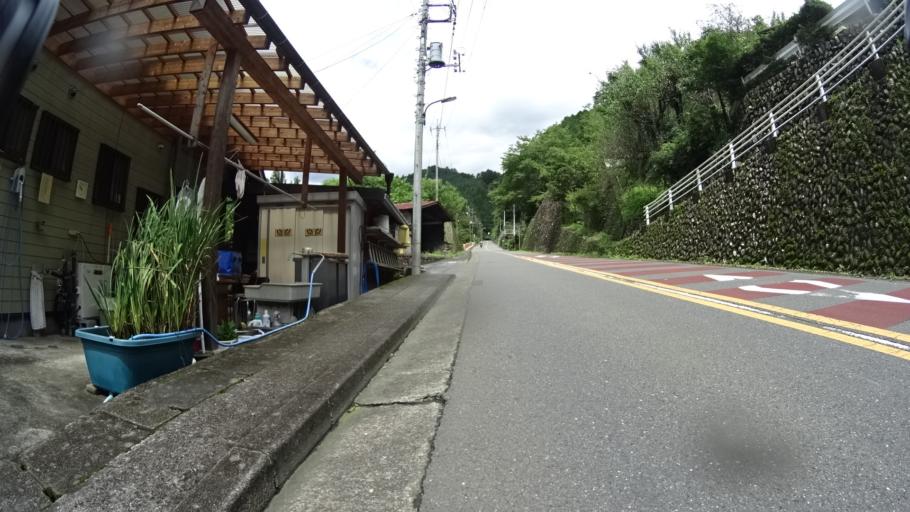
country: JP
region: Tokyo
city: Ome
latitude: 35.8370
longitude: 139.2031
